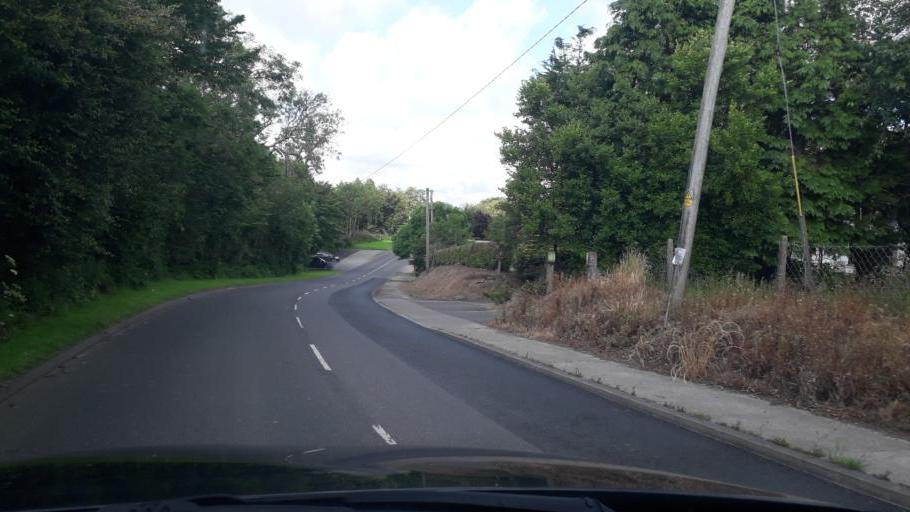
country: IE
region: Leinster
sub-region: Loch Garman
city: Loch Garman
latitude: 52.2868
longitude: -6.5246
